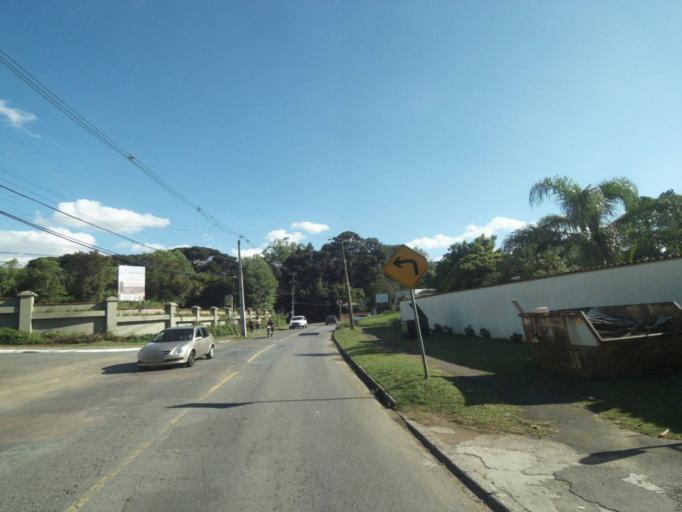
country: BR
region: Parana
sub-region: Curitiba
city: Curitiba
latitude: -25.4469
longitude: -49.3208
